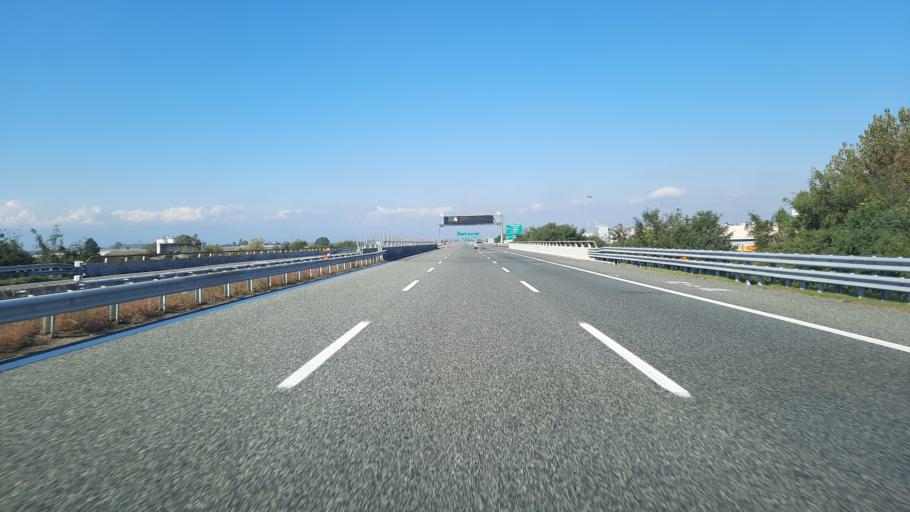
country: IT
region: Piedmont
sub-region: Provincia di Novara
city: Biandrate
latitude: 45.4562
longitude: 8.4537
